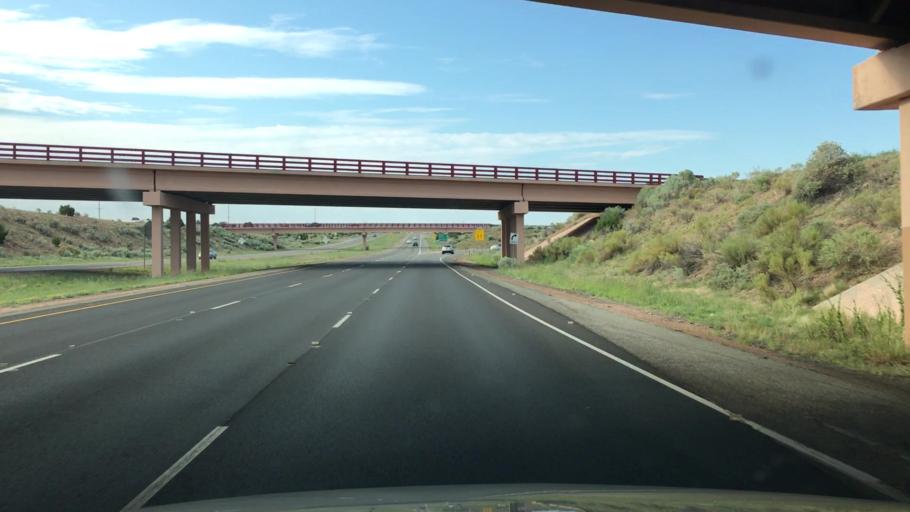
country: US
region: New Mexico
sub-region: Santa Fe County
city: Santa Fe
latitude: 35.6348
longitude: -105.9565
